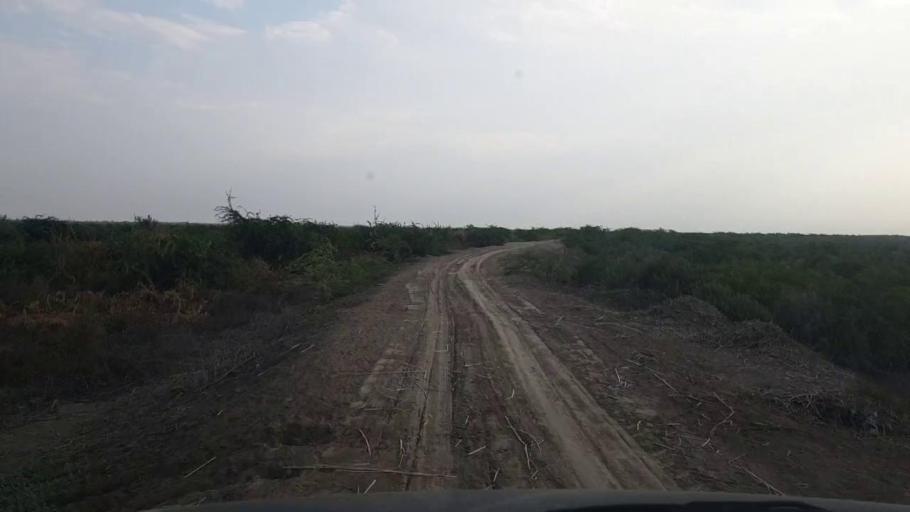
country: PK
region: Sindh
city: Badin
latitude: 24.4771
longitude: 68.7000
